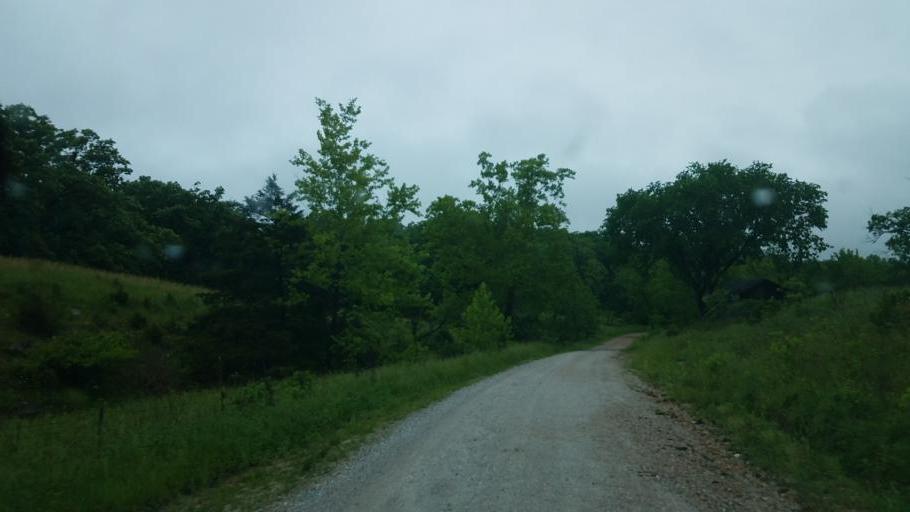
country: US
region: Missouri
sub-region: Moniteau County
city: California
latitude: 38.7258
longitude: -92.6099
